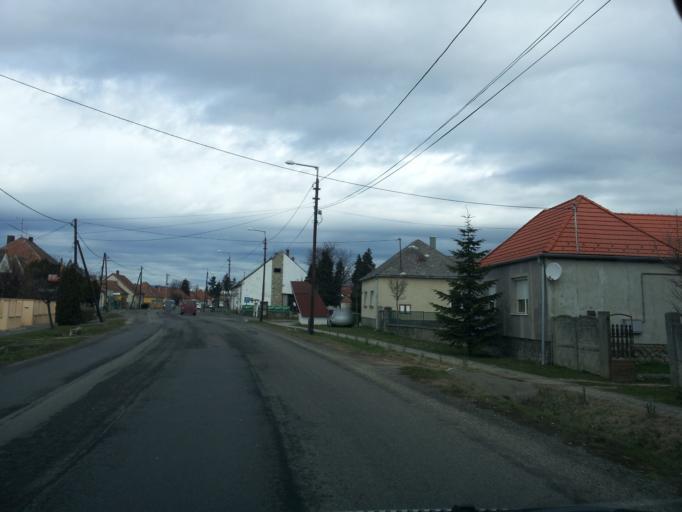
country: HU
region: Vas
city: Gencsapati
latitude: 47.3393
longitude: 16.5801
